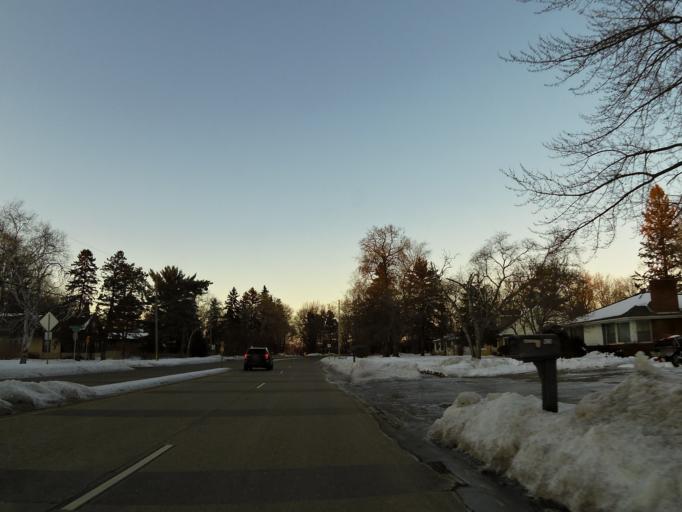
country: US
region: Minnesota
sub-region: Ramsey County
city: White Bear Lake
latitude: 45.0661
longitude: -93.0154
